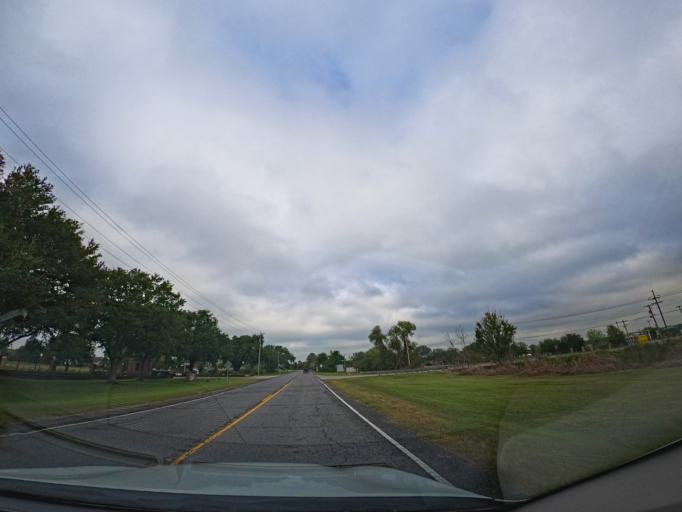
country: US
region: Louisiana
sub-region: Terrebonne Parish
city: Bayou Cane
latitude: 29.5619
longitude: -90.7936
